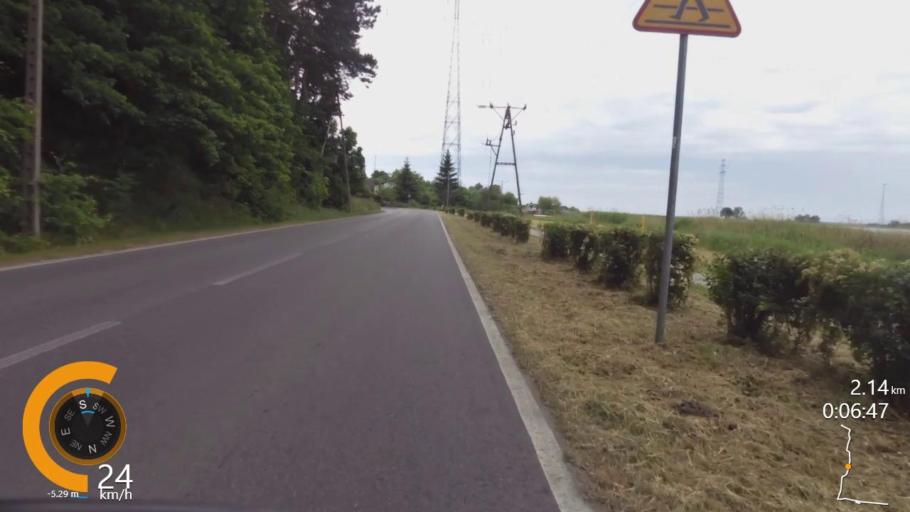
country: PL
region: West Pomeranian Voivodeship
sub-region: Powiat kamienski
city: Miedzyzdroje
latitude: 53.8947
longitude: 14.4372
